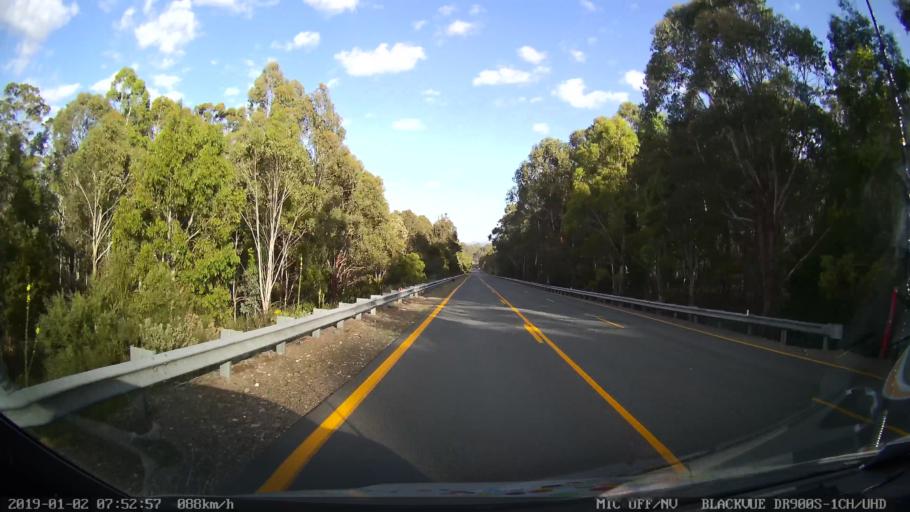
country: AU
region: New South Wales
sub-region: Tumut Shire
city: Tumut
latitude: -35.7109
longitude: 148.5123
